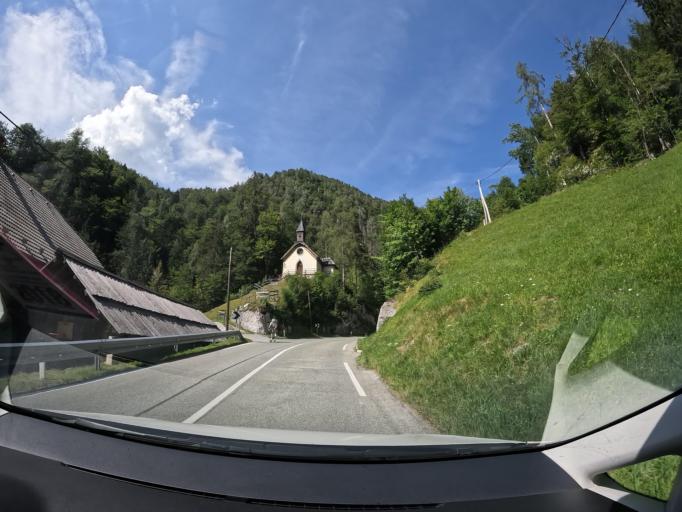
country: SI
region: Trzic
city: Trzic
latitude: 46.4124
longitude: 14.2981
